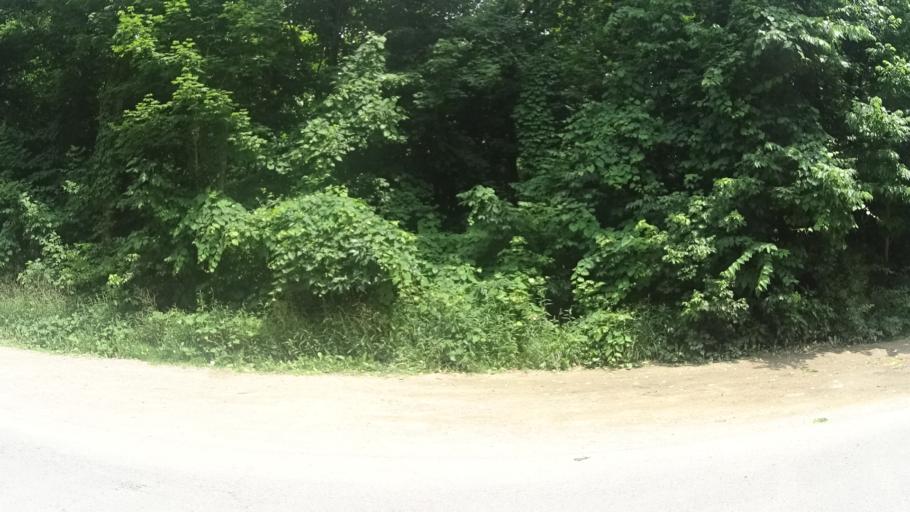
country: US
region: Ohio
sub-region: Erie County
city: Milan
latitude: 41.2873
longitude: -82.6430
